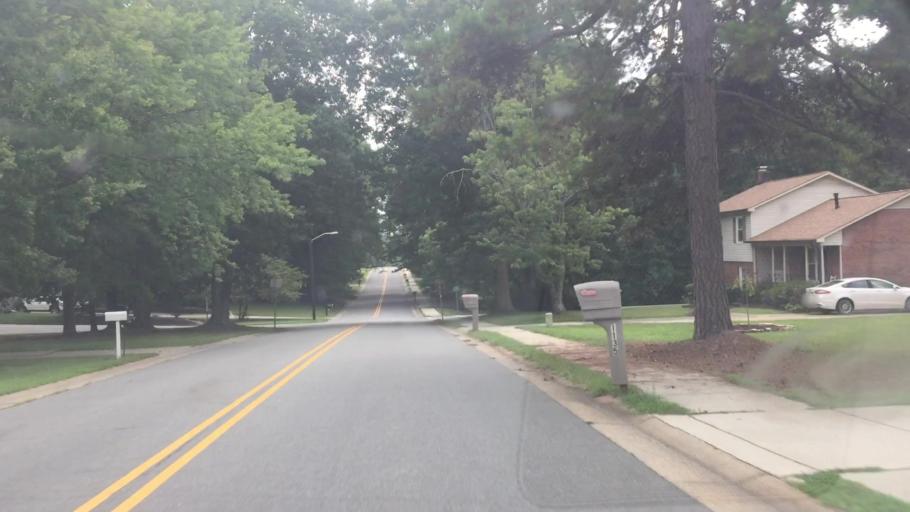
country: US
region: North Carolina
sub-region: Iredell County
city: Mooresville
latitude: 35.5573
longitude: -80.8013
